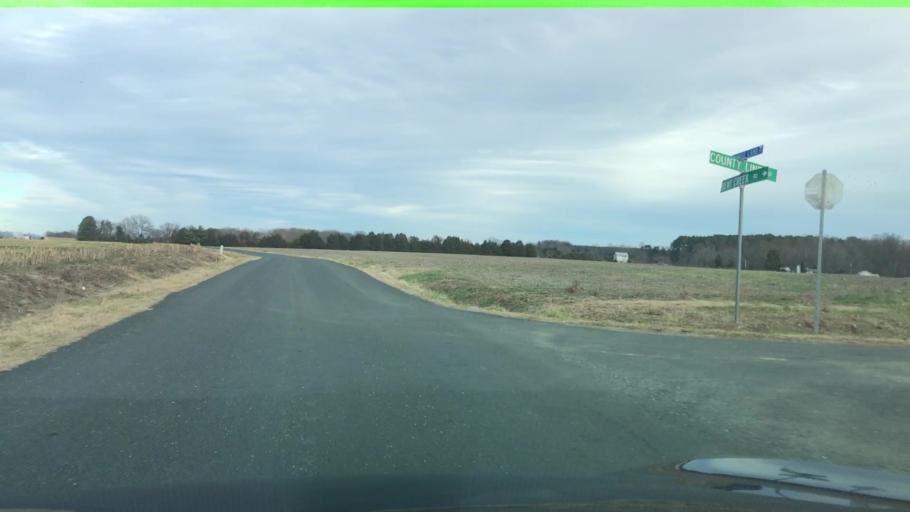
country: US
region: Virginia
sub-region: Appomattox County
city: Appomattox
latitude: 37.2464
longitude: -78.8807
